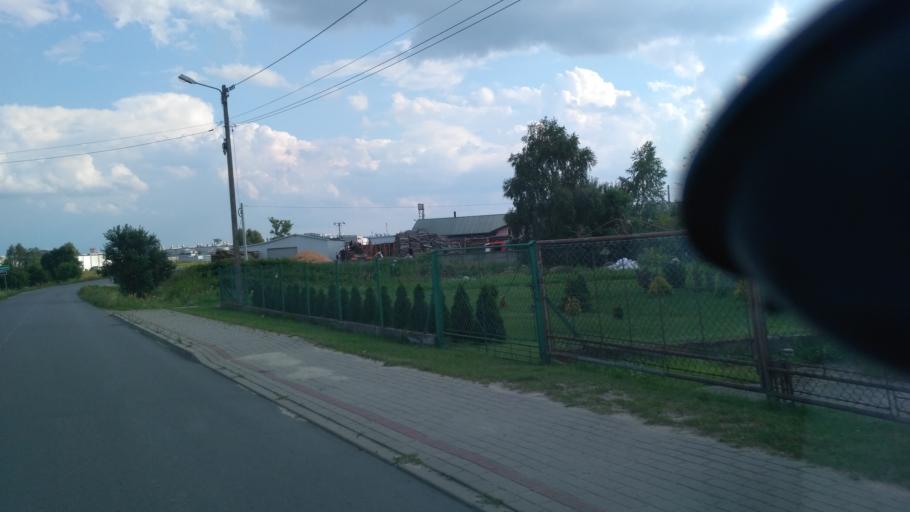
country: PL
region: Subcarpathian Voivodeship
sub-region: Powiat rzeszowski
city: Wysoka Glogowska
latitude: 50.1280
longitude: 22.0252
